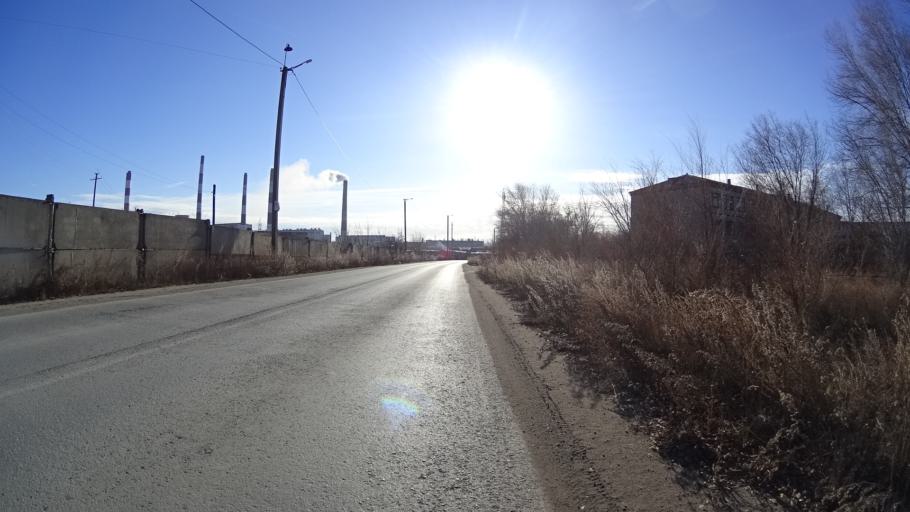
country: RU
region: Chelyabinsk
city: Troitsk
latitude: 54.0450
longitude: 61.6403
